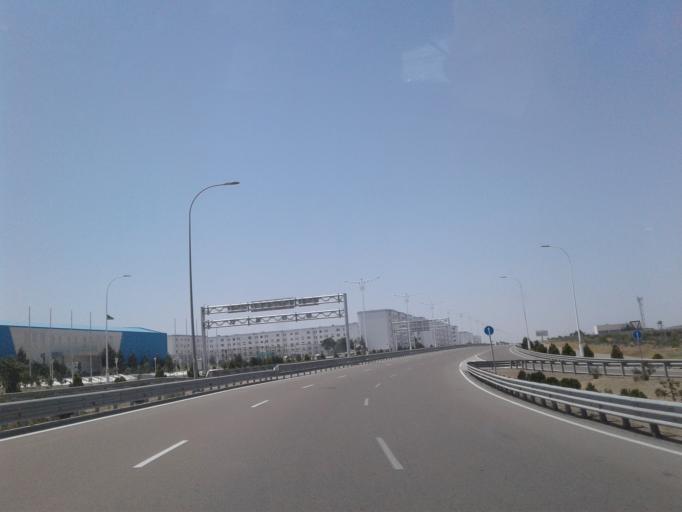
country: TM
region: Balkan
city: Turkmenbasy
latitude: 39.9819
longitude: 52.8674
